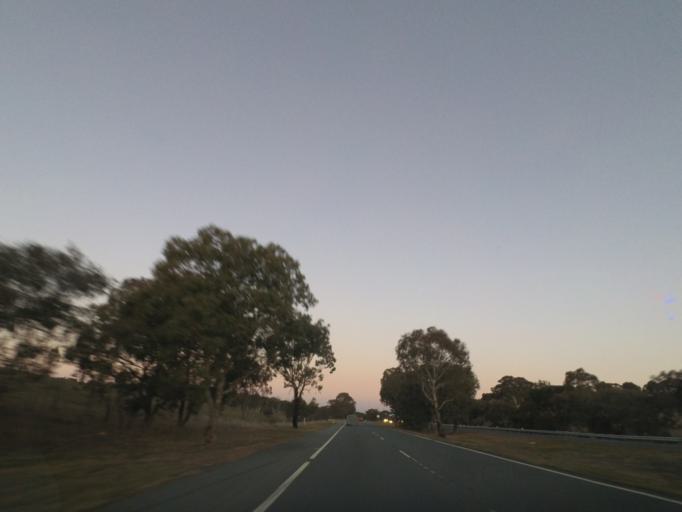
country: AU
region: Australian Capital Territory
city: Kaleen
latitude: -35.2082
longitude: 149.1060
